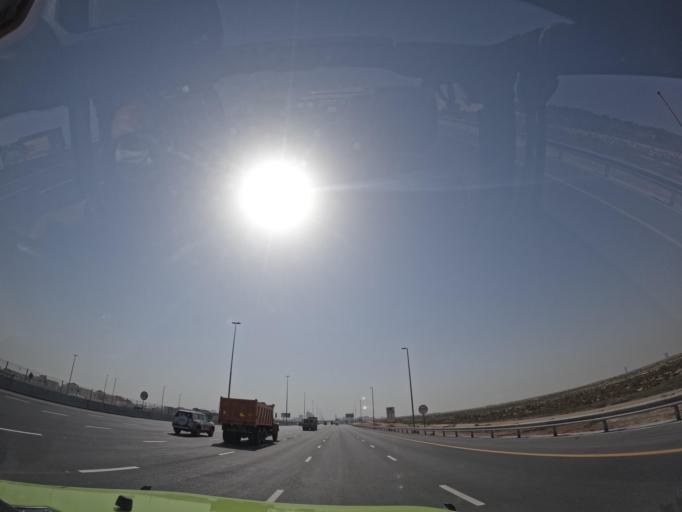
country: AE
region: Dubai
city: Dubai
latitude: 25.1415
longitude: 55.3459
